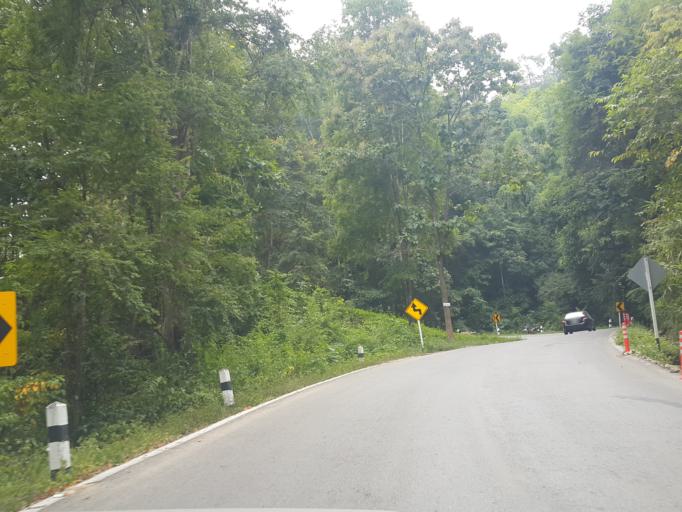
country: TH
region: Mae Hong Son
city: Mae Hi
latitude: 19.2717
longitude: 98.5005
